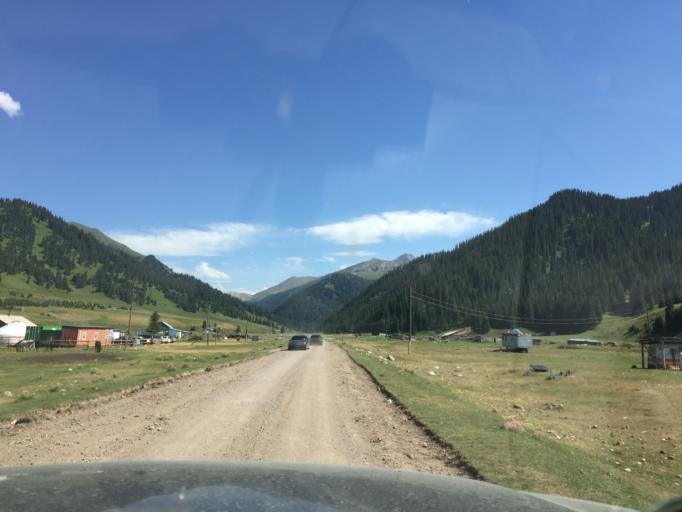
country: KZ
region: Almaty Oblysy
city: Kegen
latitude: 42.6763
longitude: 79.1978
